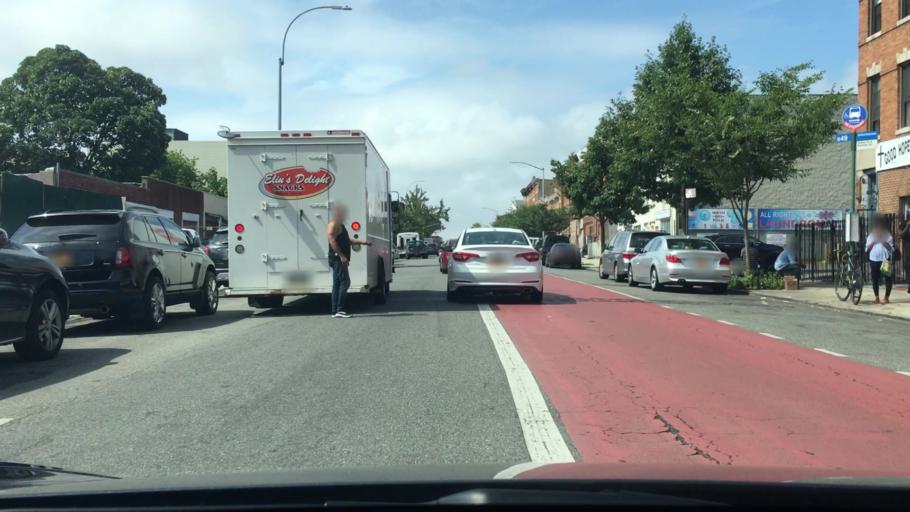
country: US
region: New York
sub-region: Kings County
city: Brooklyn
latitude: 40.6452
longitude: -73.9519
